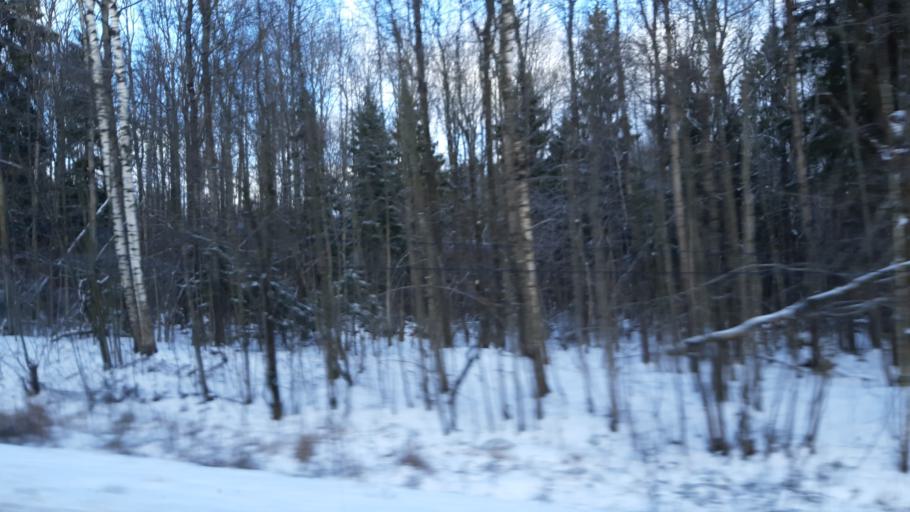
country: RU
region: Moskovskaya
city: Svatkovo
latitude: 56.3170
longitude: 38.3031
